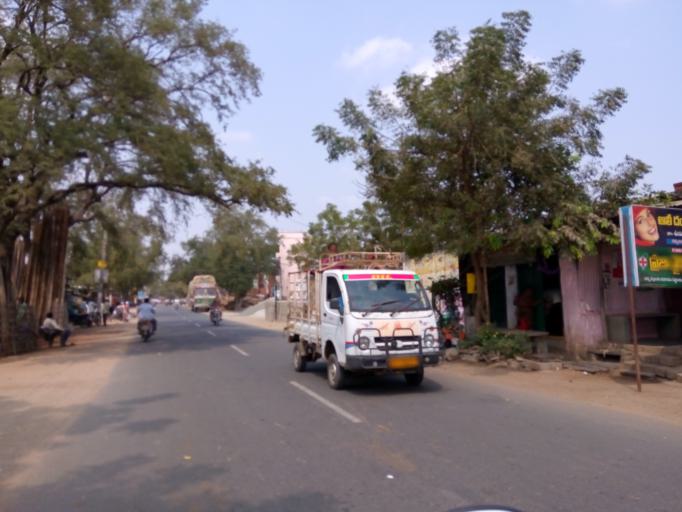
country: IN
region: Andhra Pradesh
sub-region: Prakasam
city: pedda nakkalapalem
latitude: 15.9637
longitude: 80.2786
